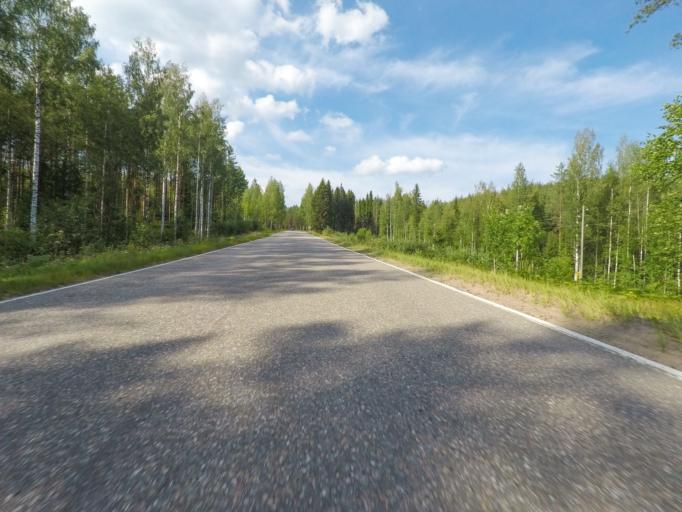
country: FI
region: Southern Savonia
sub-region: Mikkeli
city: Puumala
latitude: 61.6816
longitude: 28.2307
